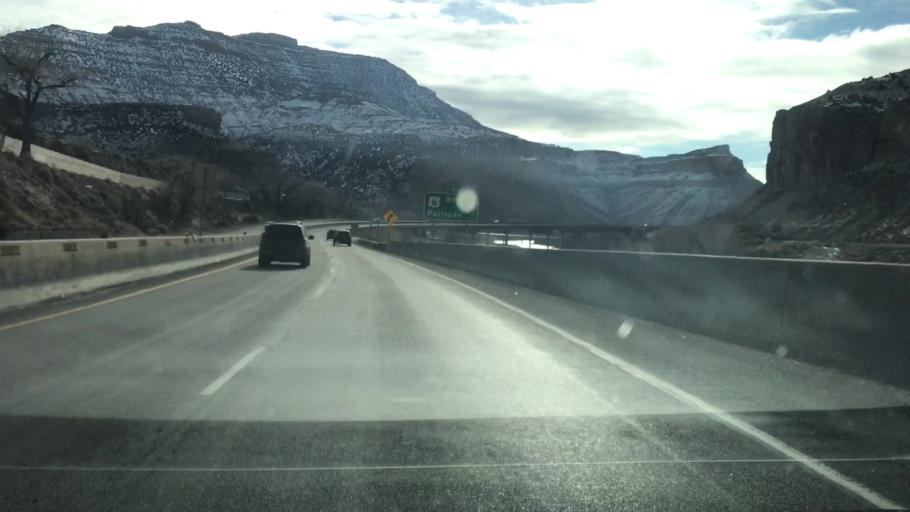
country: US
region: Colorado
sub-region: Mesa County
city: Palisade
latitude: 39.1282
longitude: -108.3249
